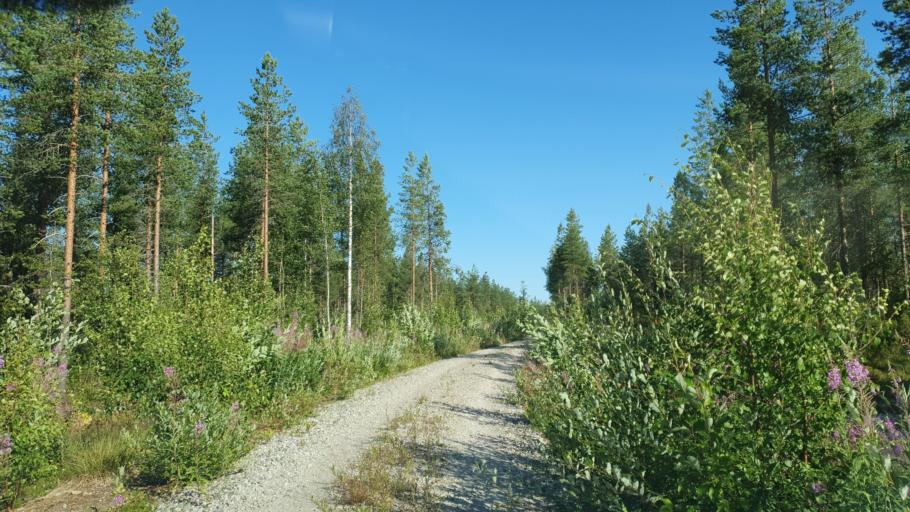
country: FI
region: Kainuu
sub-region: Kehys-Kainuu
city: Kuhmo
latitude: 64.0019
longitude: 29.7495
